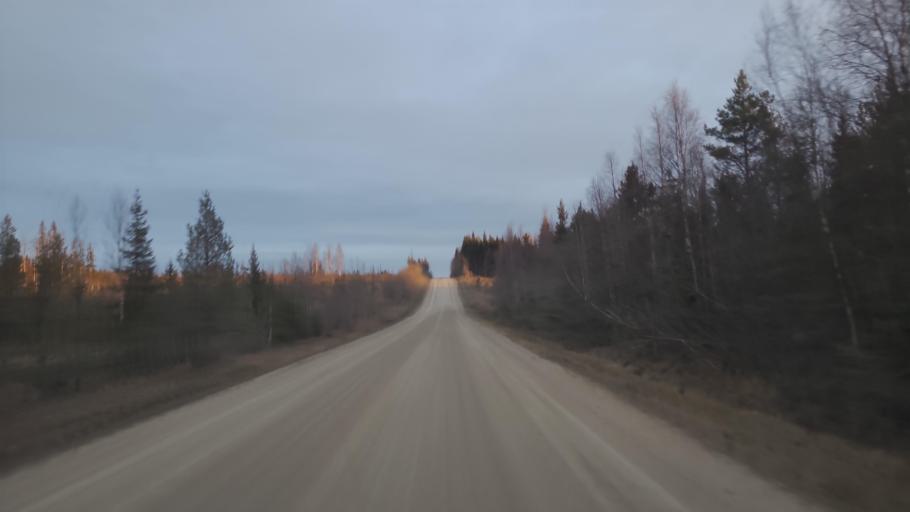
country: FI
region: Lapland
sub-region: Kemi-Tornio
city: Tervola
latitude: 66.0615
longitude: 24.9282
